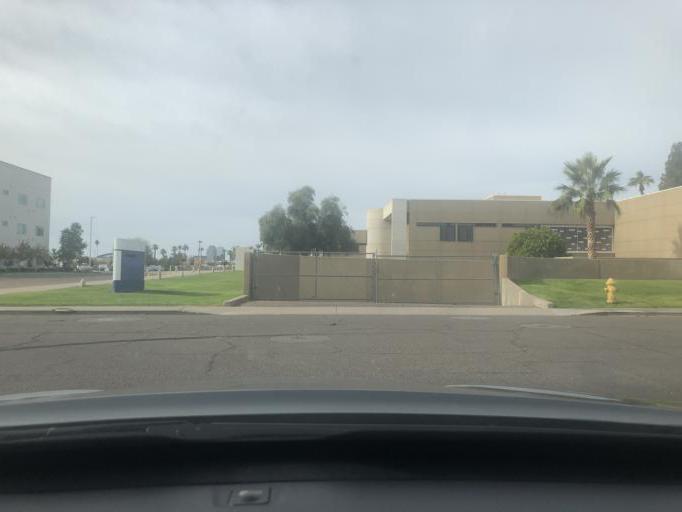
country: US
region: Arizona
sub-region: Maricopa County
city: Phoenix
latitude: 33.4530
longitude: -112.0411
